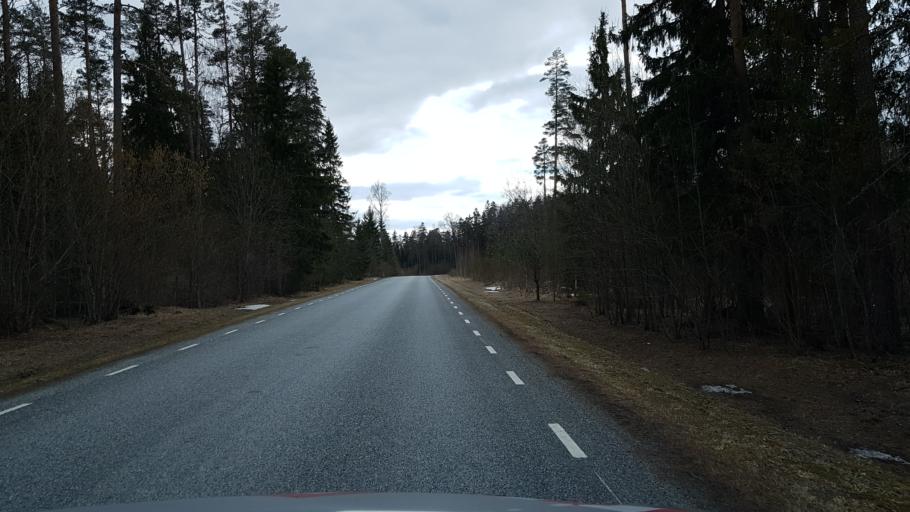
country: EE
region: Laeaene-Virumaa
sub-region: Tamsalu vald
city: Tamsalu
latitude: 59.2346
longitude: 26.1719
